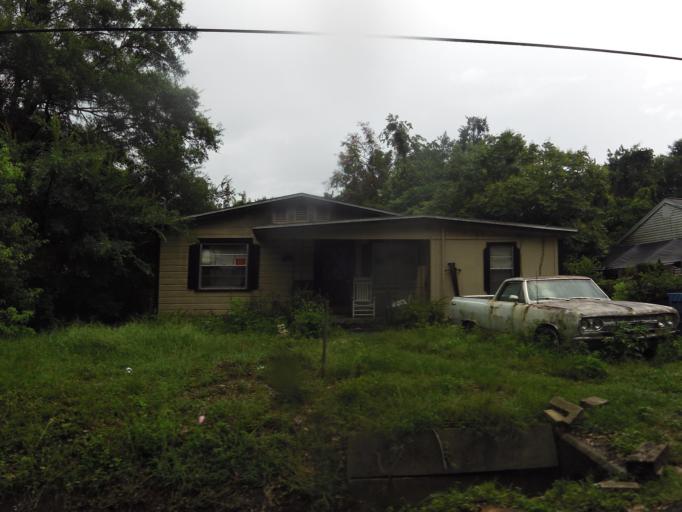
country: US
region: Florida
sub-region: Duval County
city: Jacksonville
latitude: 30.4656
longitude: -81.6295
